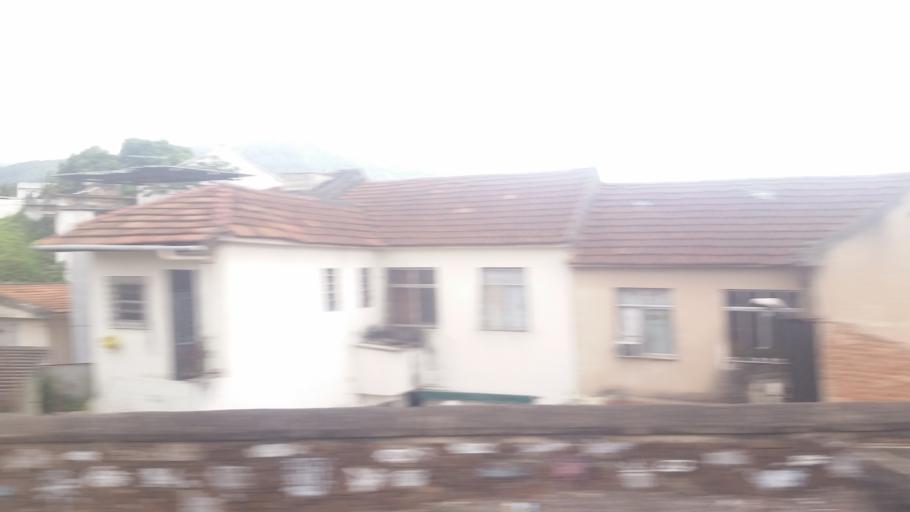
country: BR
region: Rio de Janeiro
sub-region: Rio De Janeiro
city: Rio de Janeiro
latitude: -22.8951
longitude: -43.3027
